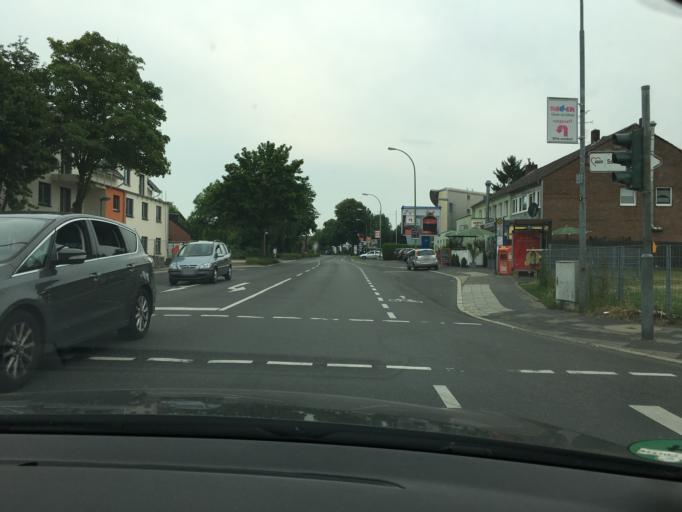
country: DE
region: North Rhine-Westphalia
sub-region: Regierungsbezirk Koln
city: Kerpen
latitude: 50.8758
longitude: 6.6929
